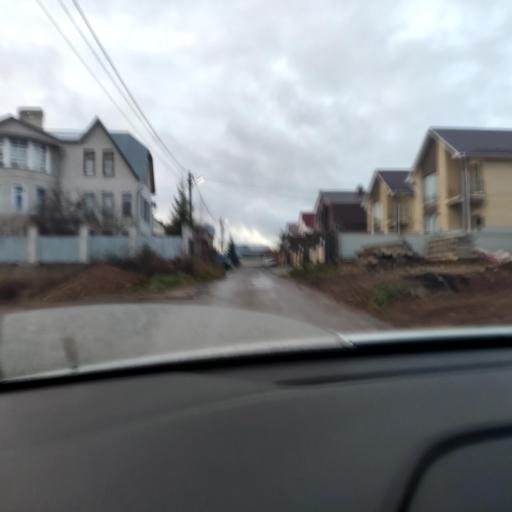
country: RU
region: Tatarstan
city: Stolbishchi
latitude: 55.7553
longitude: 49.2919
